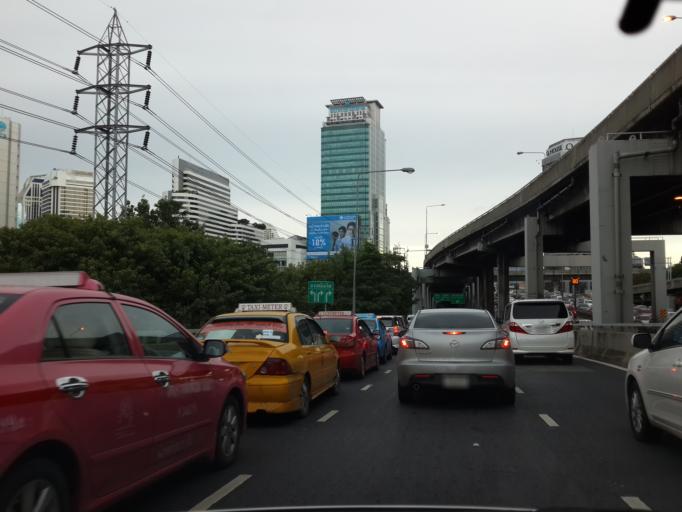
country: TH
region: Bangkok
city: Ratchathewi
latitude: 13.7451
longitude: 100.5503
